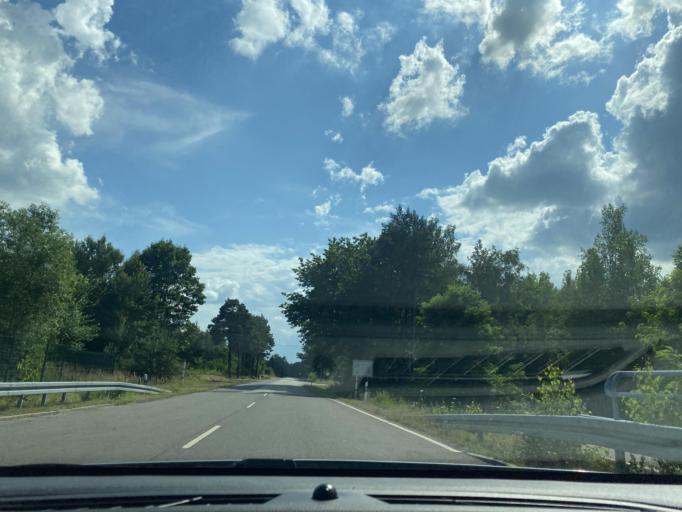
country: DE
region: Saxony
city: Boxberg
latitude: 51.4219
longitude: 14.5911
